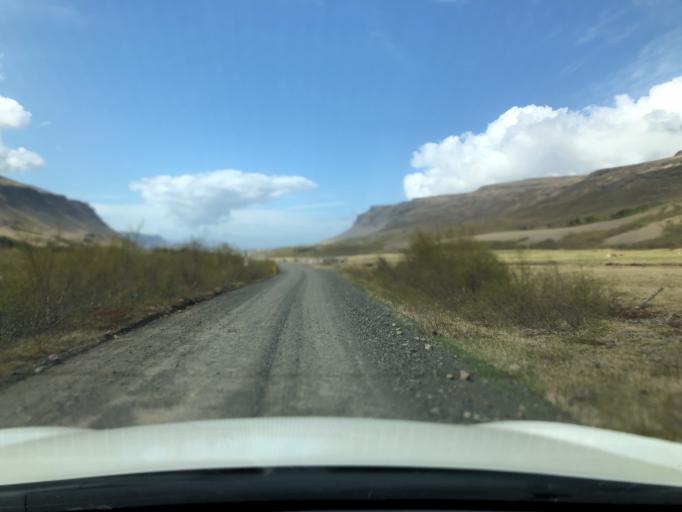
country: IS
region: South
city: Hveragerdi
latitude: 64.3860
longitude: -21.3133
